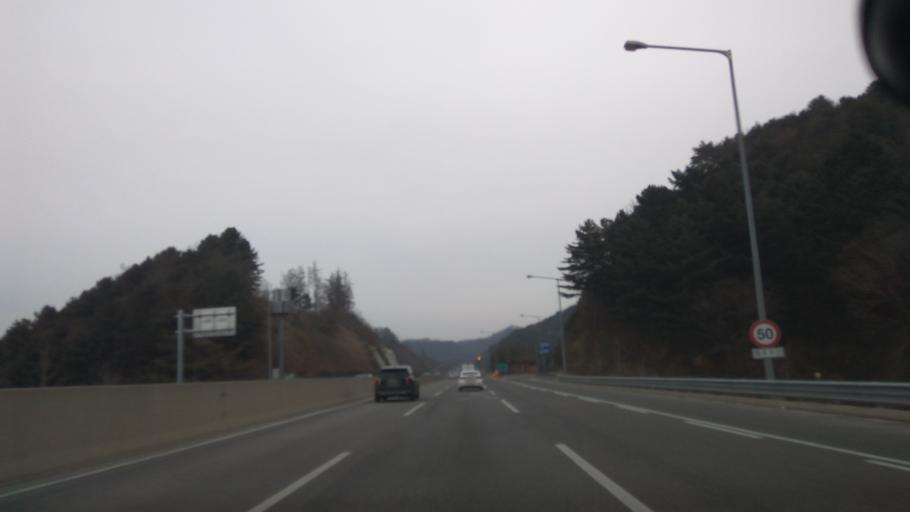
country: KR
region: Gangwon-do
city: Sindong
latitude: 37.7328
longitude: 127.6200
